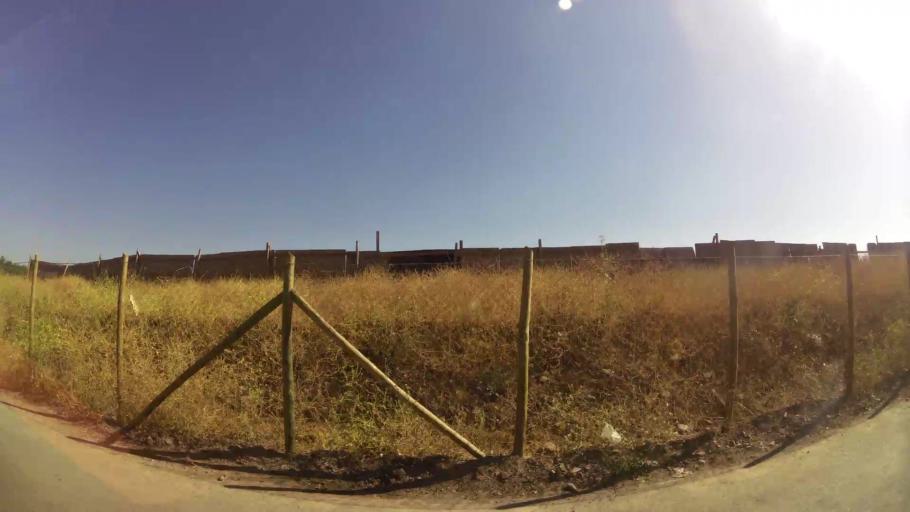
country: CL
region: Santiago Metropolitan
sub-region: Provincia de Maipo
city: San Bernardo
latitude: -33.6097
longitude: -70.6751
